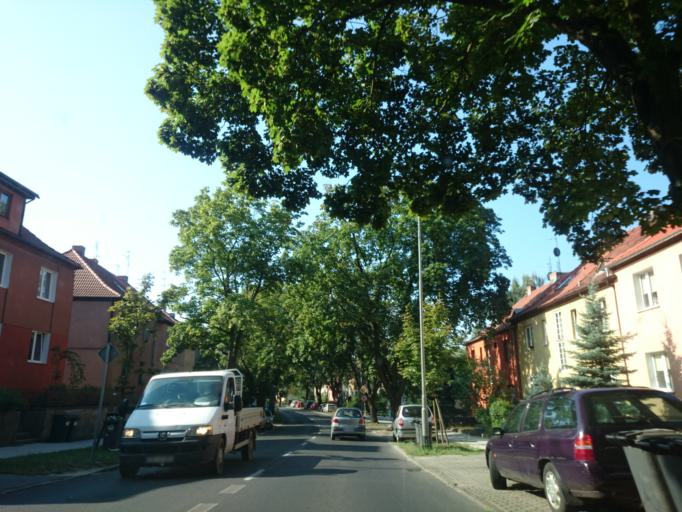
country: PL
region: West Pomeranian Voivodeship
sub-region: Szczecin
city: Szczecin
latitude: 53.4365
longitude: 14.5122
